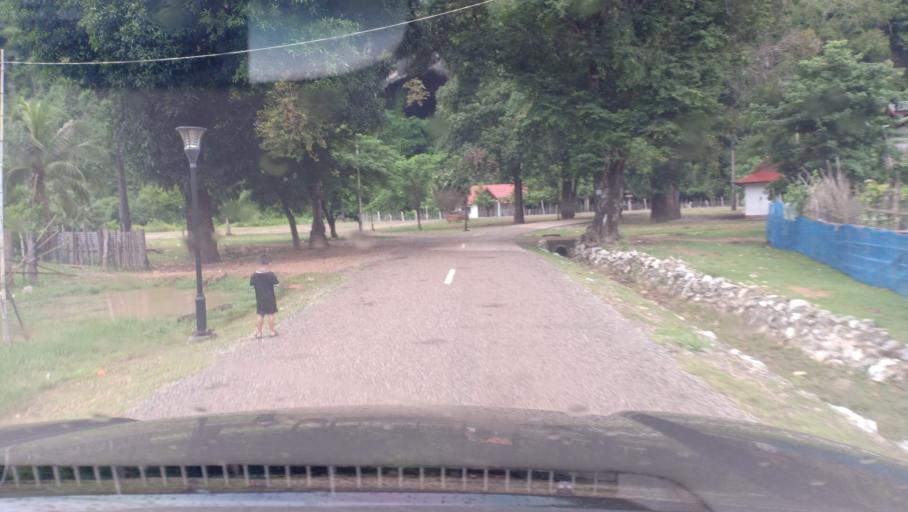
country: LA
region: Khammouan
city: Thakhek
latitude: 17.4295
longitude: 104.8642
